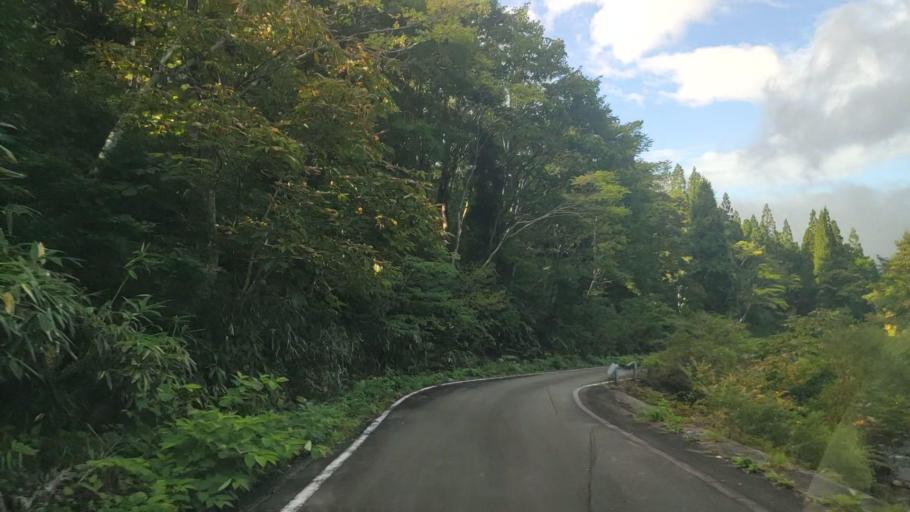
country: JP
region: Toyama
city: Yatsuomachi-higashikumisaka
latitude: 36.3666
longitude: 137.0751
